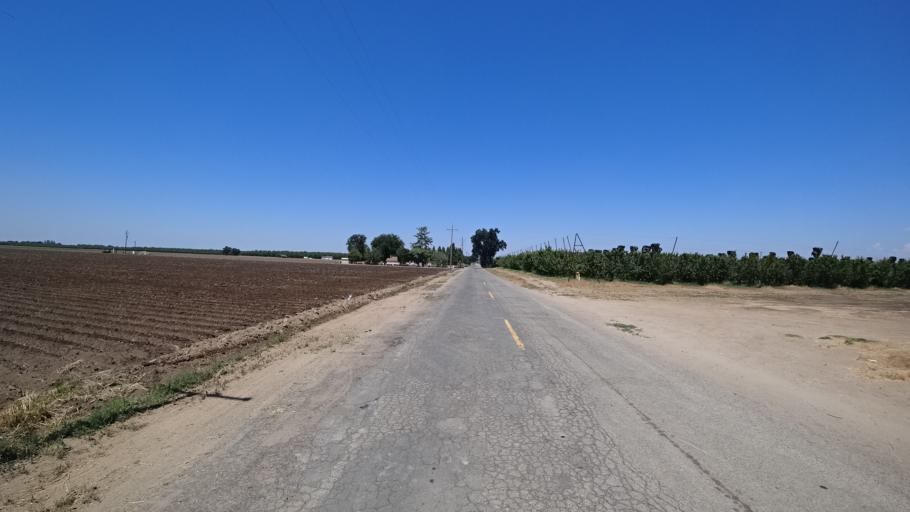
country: US
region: California
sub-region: Kings County
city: Lucerne
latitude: 36.4073
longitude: -119.6010
